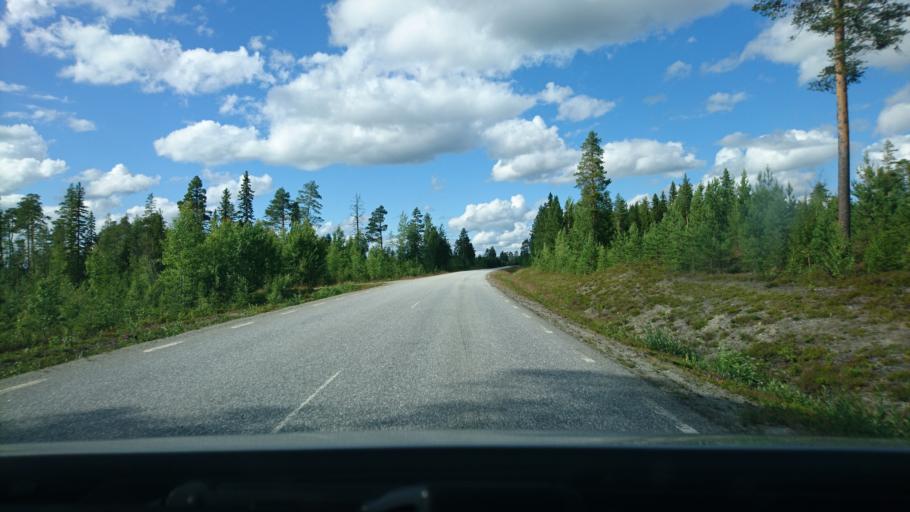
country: SE
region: Vaesterbotten
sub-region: Asele Kommun
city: Asele
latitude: 64.0515
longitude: 17.2819
